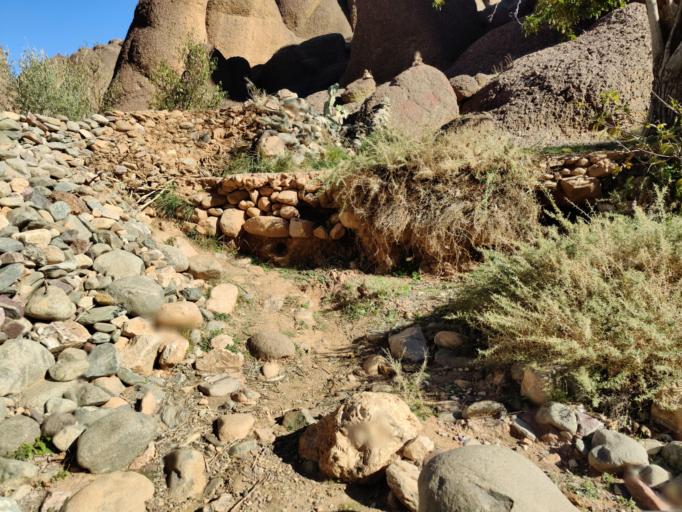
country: MA
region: Souss-Massa-Draa
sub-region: Taroudannt
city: Taliouine
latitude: 30.5551
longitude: -7.5929
